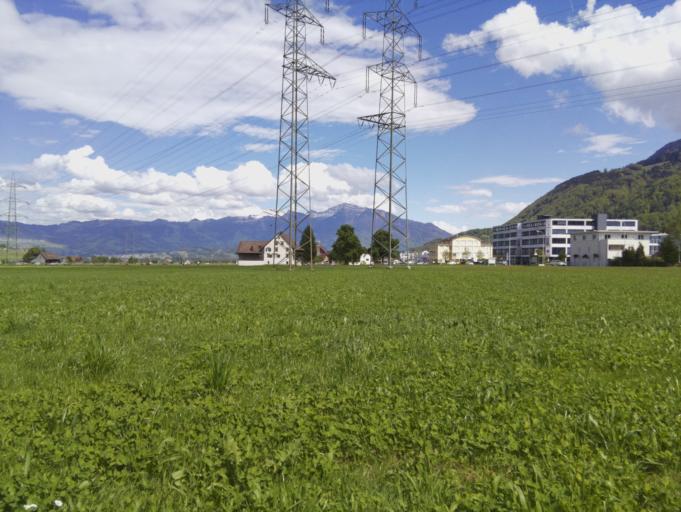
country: CH
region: Schwyz
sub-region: Bezirk March
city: Schubelbach
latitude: 47.1767
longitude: 8.9088
